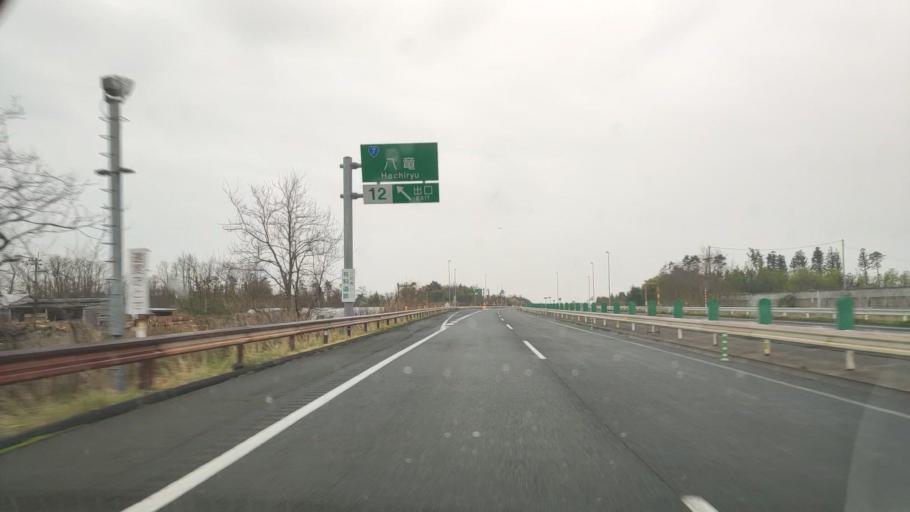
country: JP
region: Akita
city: Noshiromachi
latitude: 40.1223
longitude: 140.0121
